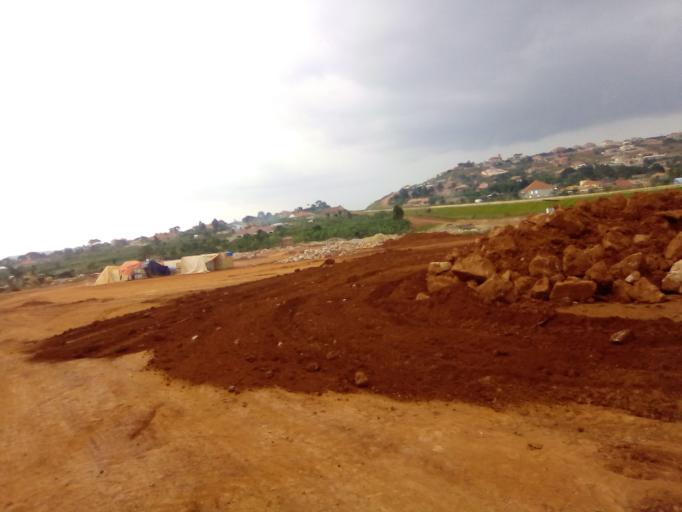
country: UG
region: Central Region
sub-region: Wakiso District
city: Kajansi
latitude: 0.1665
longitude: 32.5127
